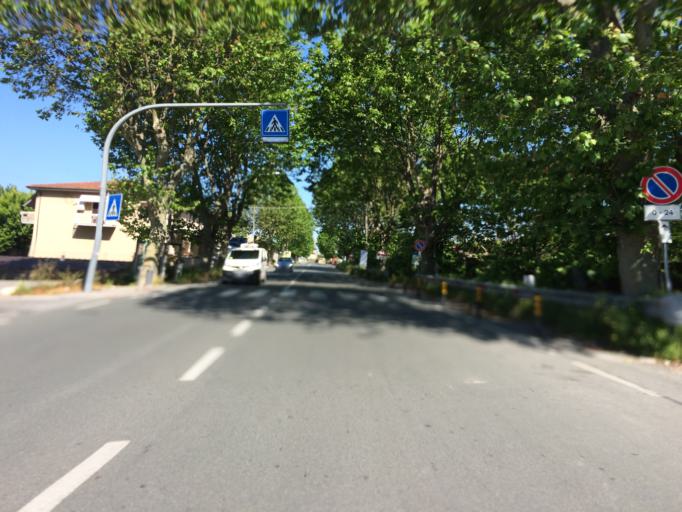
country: IT
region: Liguria
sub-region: Provincia di La Spezia
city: Colombiera-Molicciara
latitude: 44.0853
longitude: 10.0056
